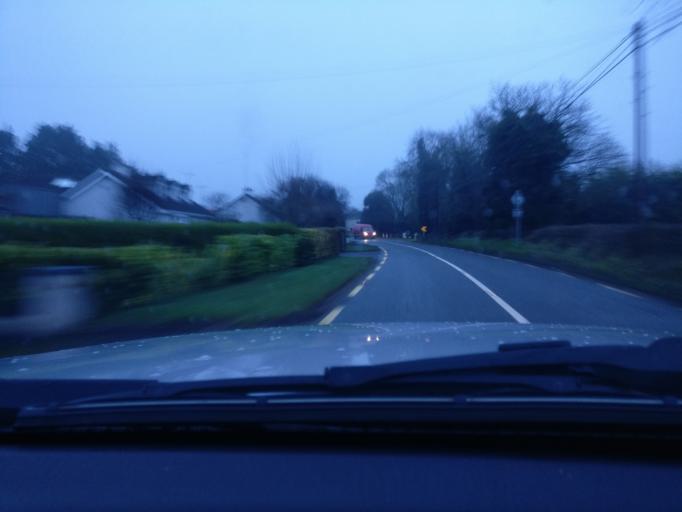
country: IE
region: Leinster
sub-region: An Mhi
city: Athboy
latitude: 53.6118
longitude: -6.9459
